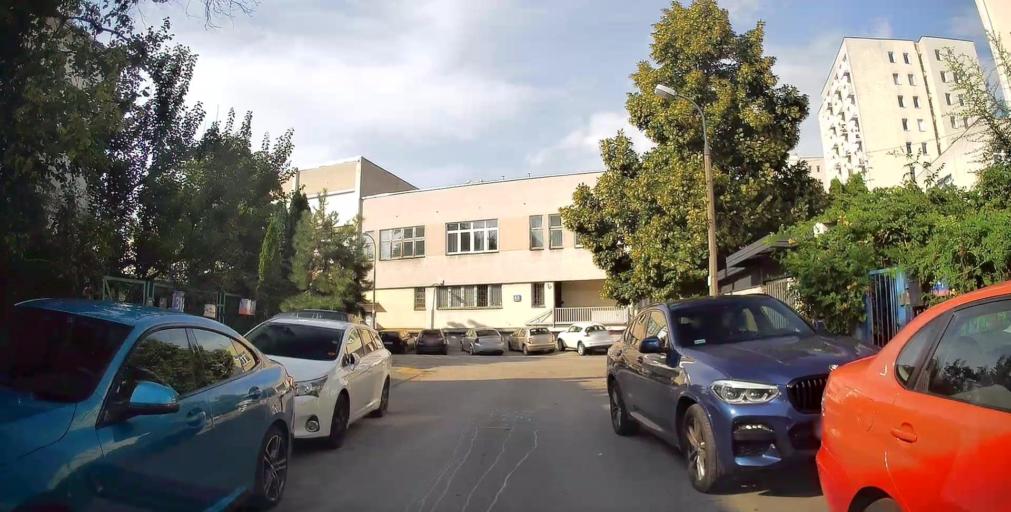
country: PL
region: Masovian Voivodeship
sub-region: Warszawa
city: Ochota
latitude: 52.1904
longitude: 20.9914
